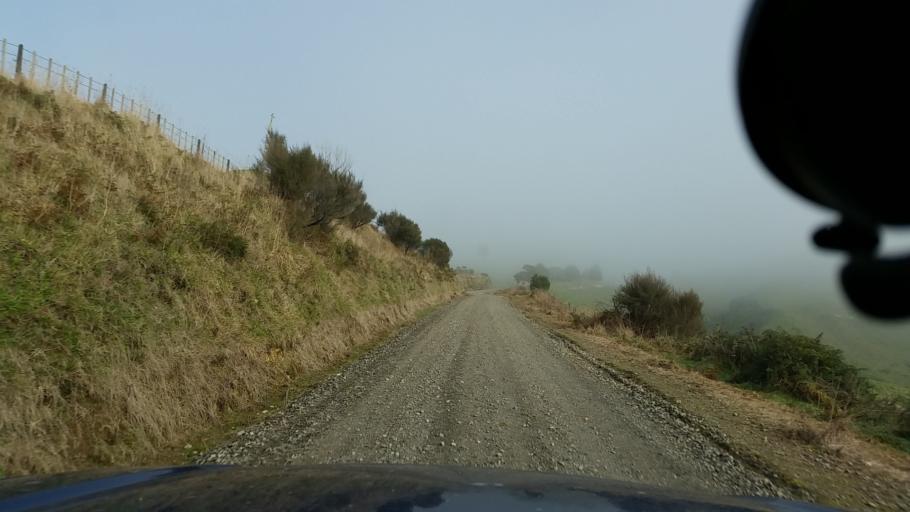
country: NZ
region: Taranaki
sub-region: New Plymouth District
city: Waitara
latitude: -38.9983
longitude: 174.7707
